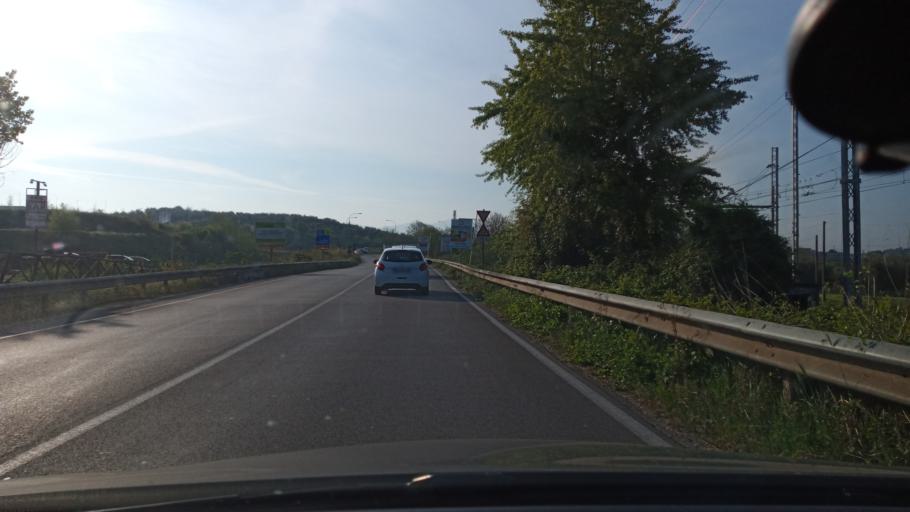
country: IT
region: Latium
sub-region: Citta metropolitana di Roma Capitale
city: Fiano Romano
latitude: 42.1640
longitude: 12.6448
